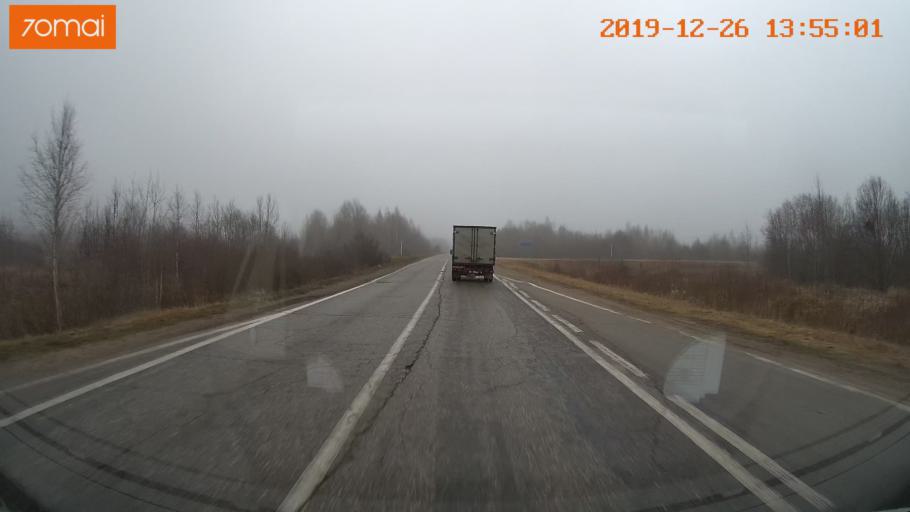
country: RU
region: Jaroslavl
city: Poshekhon'ye
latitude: 58.6077
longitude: 38.6423
